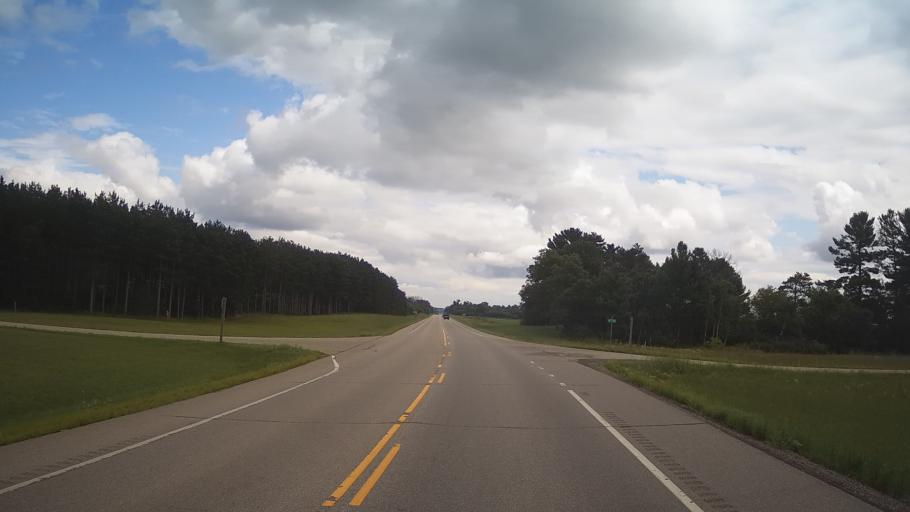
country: US
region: Wisconsin
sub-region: Adams County
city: Friendship
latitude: 44.0220
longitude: -89.6591
